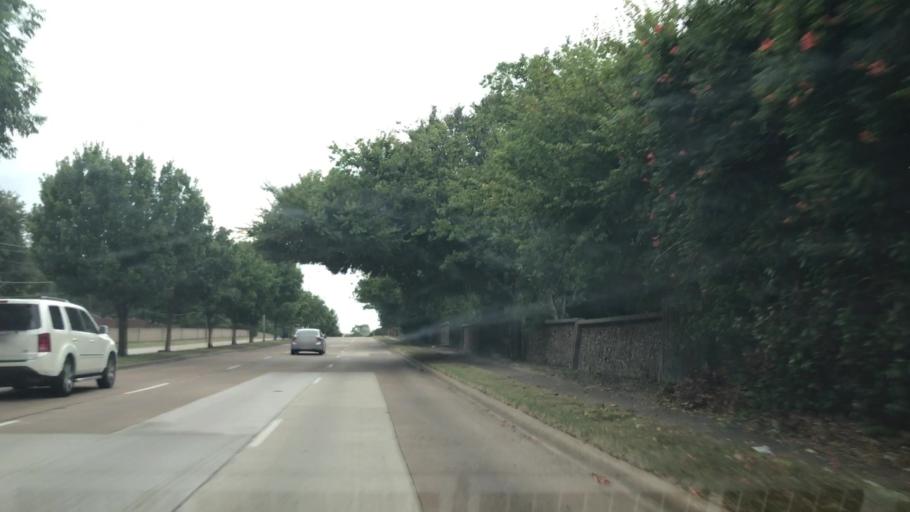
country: US
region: Texas
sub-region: Dallas County
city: Addison
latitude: 32.9501
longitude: -96.7878
